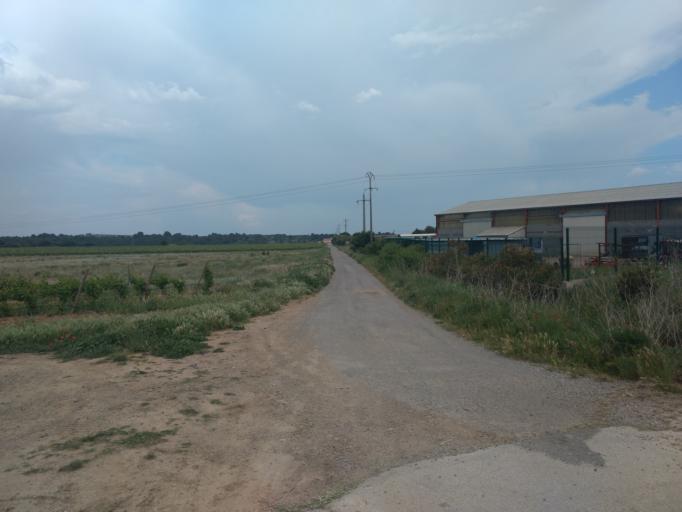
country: FR
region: Languedoc-Roussillon
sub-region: Departement de l'Aude
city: Canet
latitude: 43.2561
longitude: 2.8243
